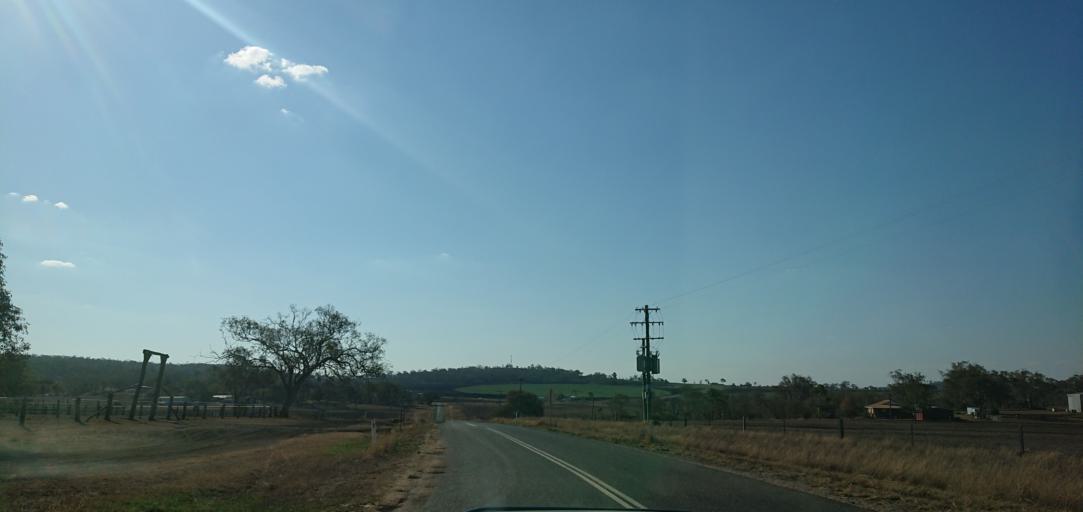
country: AU
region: Queensland
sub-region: Toowoomba
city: Westbrook
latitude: -27.7165
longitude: 151.7202
